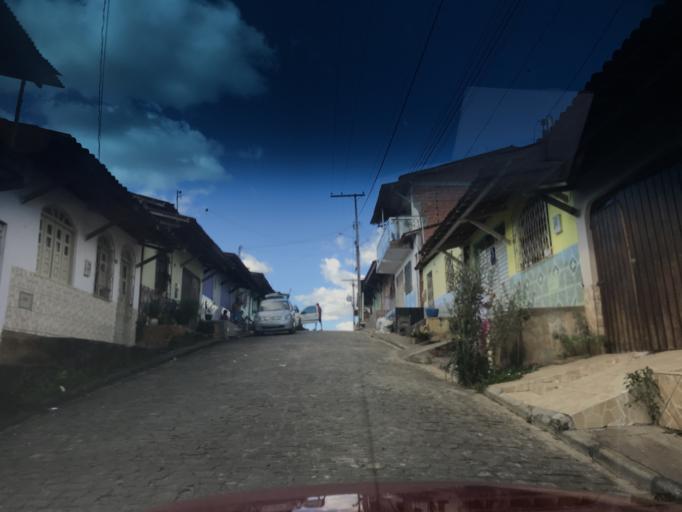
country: BR
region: Bahia
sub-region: Gandu
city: Gandu
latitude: -13.7470
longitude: -39.4939
